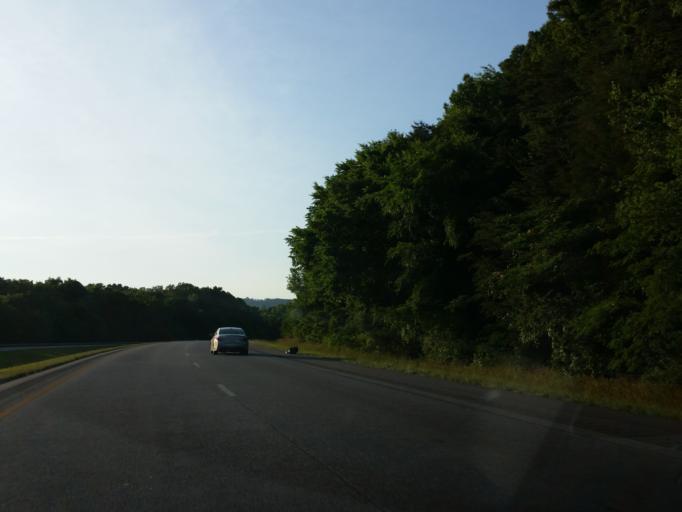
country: US
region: Georgia
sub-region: Dade County
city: Trenton
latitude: 34.7959
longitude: -85.5484
